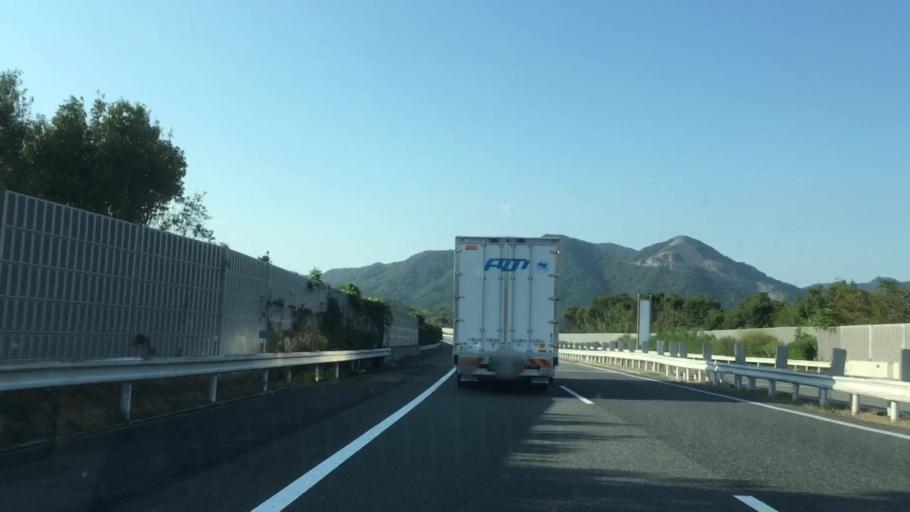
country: JP
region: Yamaguchi
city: Hofu
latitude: 34.0679
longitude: 131.4997
